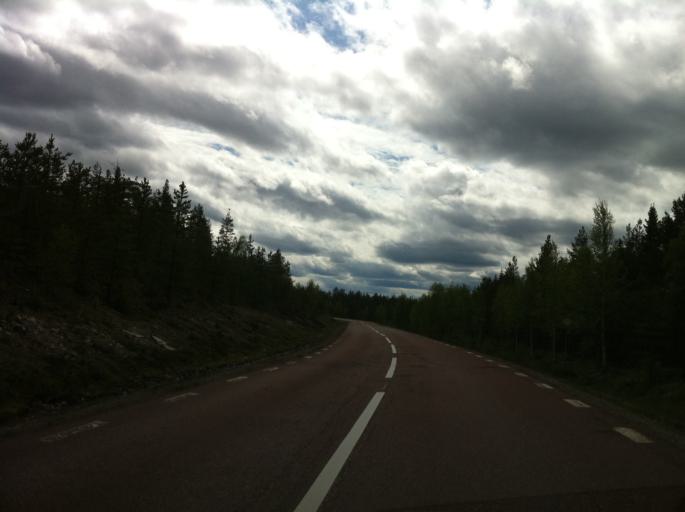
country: NO
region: Hedmark
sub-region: Trysil
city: Innbygda
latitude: 61.6089
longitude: 13.1248
